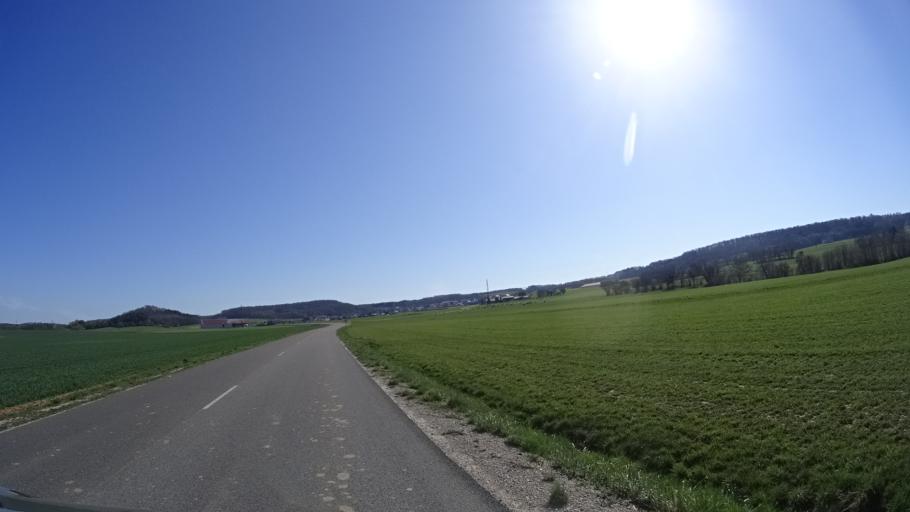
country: FR
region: Franche-Comte
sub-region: Departement du Doubs
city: Ornans
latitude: 47.1553
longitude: 6.0910
